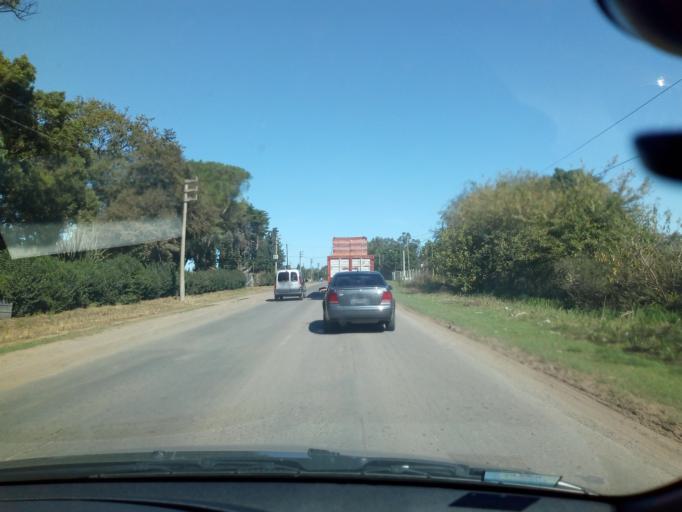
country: AR
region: Buenos Aires
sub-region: Partido de La Plata
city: La Plata
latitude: -34.9946
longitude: -58.0101
